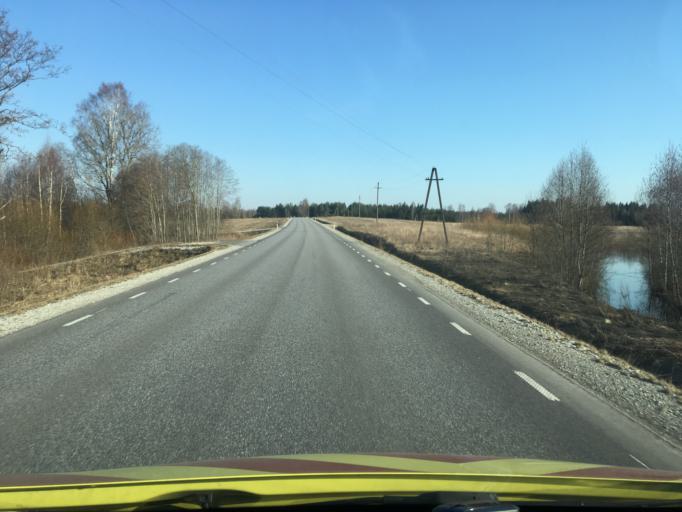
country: EE
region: Raplamaa
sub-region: Rapla vald
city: Rapla
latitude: 59.0022
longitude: 24.8426
